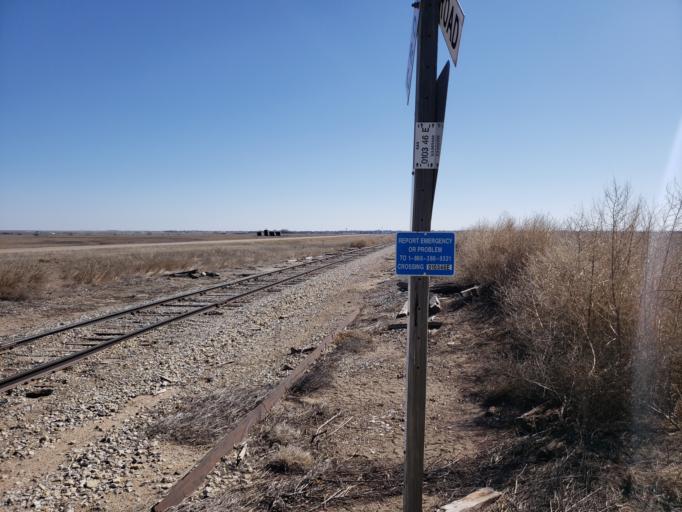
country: US
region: Kansas
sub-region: Ness County
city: Ness City
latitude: 38.4514
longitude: -99.9537
